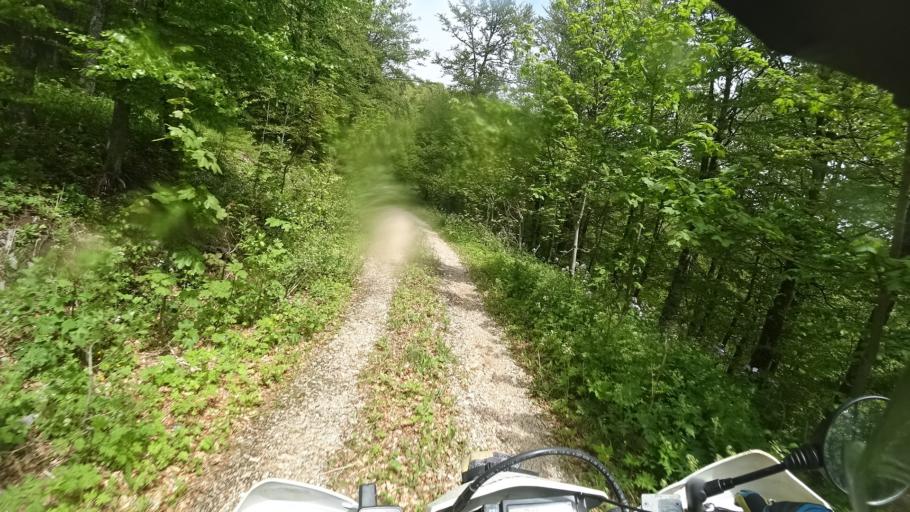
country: BA
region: Federation of Bosnia and Herzegovina
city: Orasac
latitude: 44.5682
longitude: 15.8784
